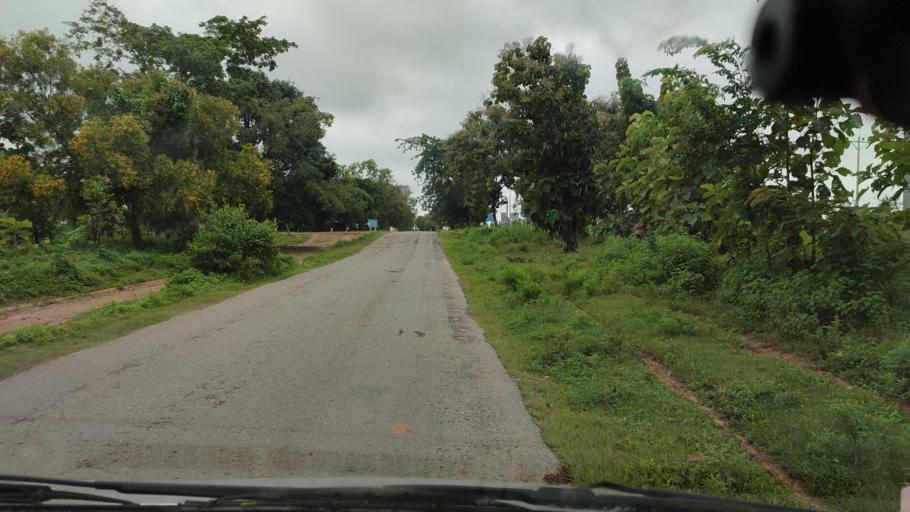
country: MM
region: Bago
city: Pyay
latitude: 18.8826
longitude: 95.4564
